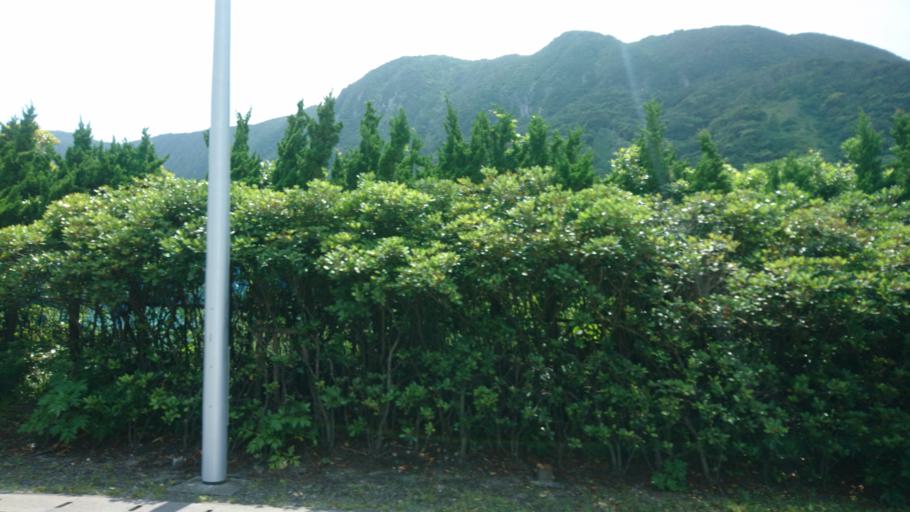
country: JP
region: Shizuoka
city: Shimoda
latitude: 34.4103
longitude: 139.2783
